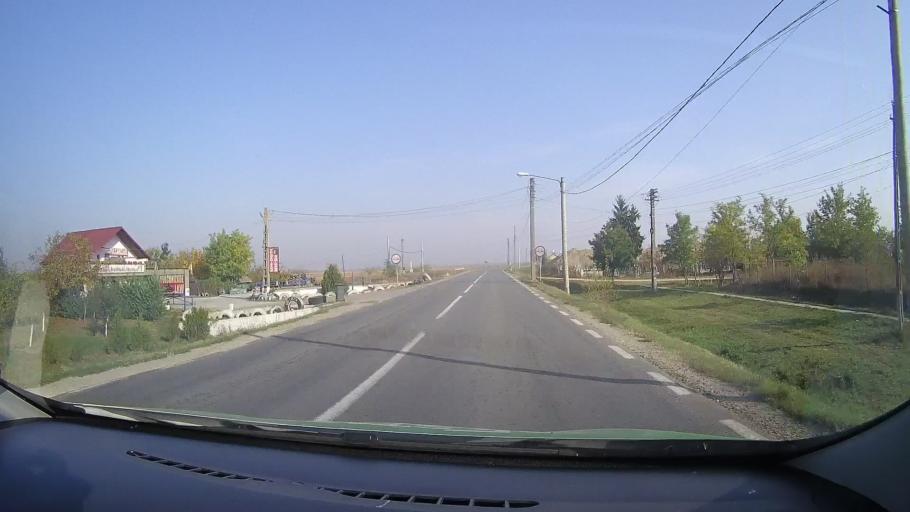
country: RO
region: Arad
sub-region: Comuna Pilu
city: Pilu
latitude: 46.5821
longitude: 21.3436
